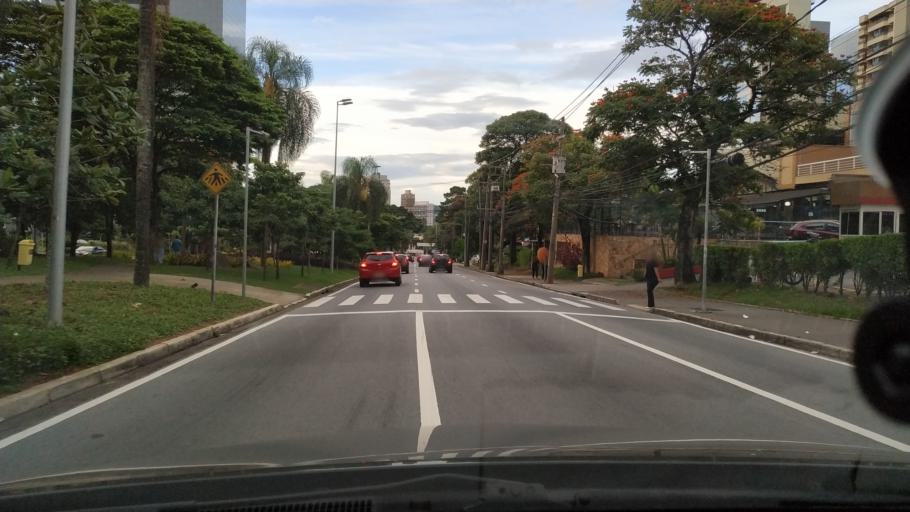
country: BR
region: Sao Paulo
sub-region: Carapicuiba
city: Carapicuiba
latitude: -23.4945
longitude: -46.8488
